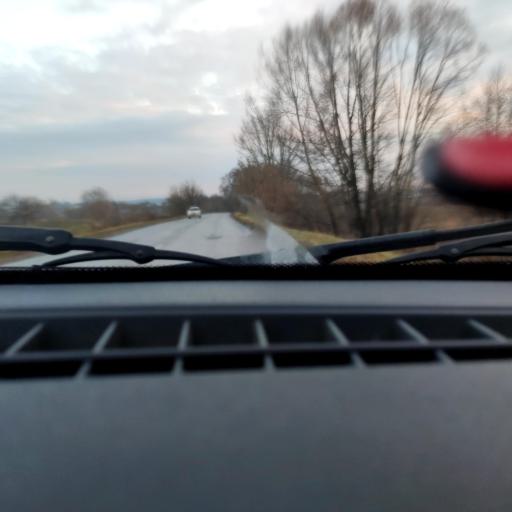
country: RU
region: Bashkortostan
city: Avdon
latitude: 54.5054
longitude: 55.8777
